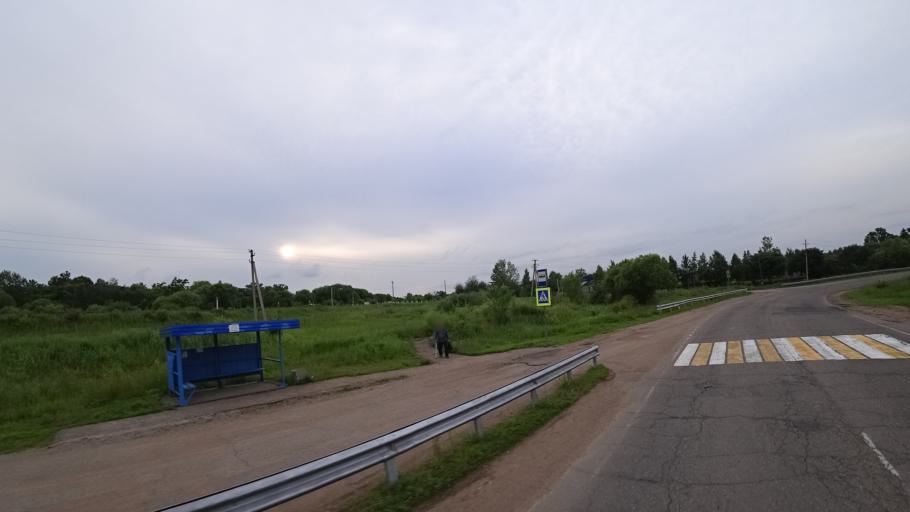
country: RU
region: Primorskiy
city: Novosysoyevka
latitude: 44.2263
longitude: 133.3509
